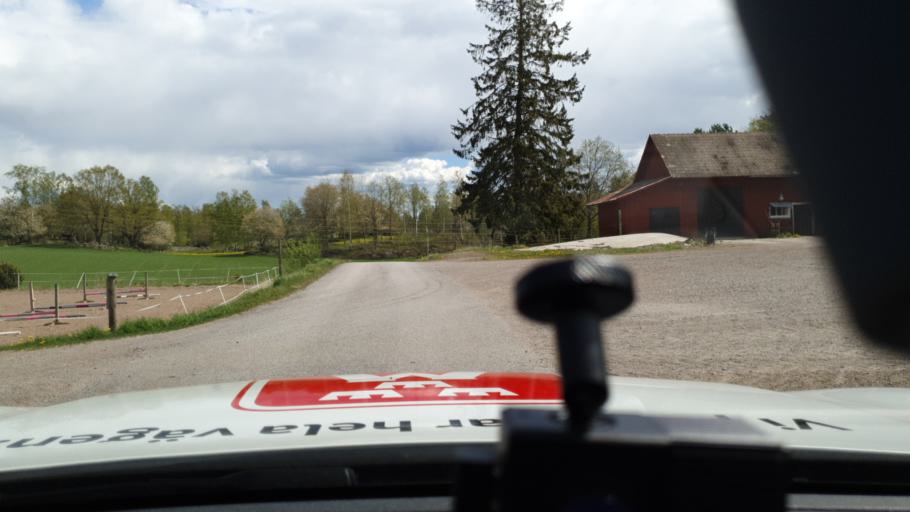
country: SE
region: Kalmar
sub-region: Vasterviks Kommun
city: Ankarsrum
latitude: 57.7810
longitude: 16.1517
